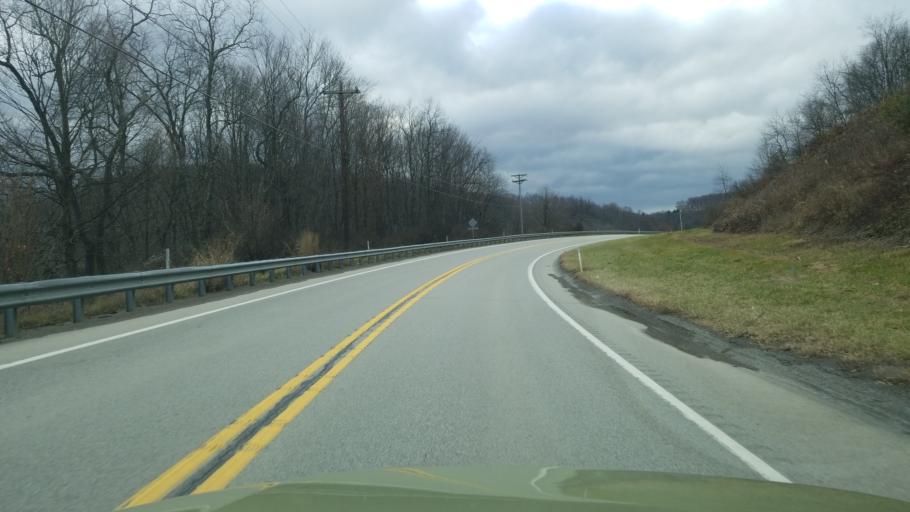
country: US
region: Pennsylvania
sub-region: Indiana County
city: Clymer
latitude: 40.8107
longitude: -79.0518
